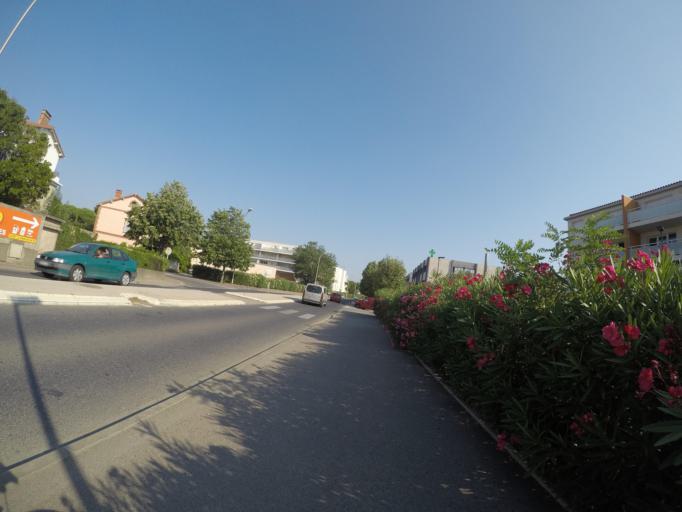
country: FR
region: Languedoc-Roussillon
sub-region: Departement des Pyrenees-Orientales
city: Thuir
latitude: 42.6294
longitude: 2.7609
